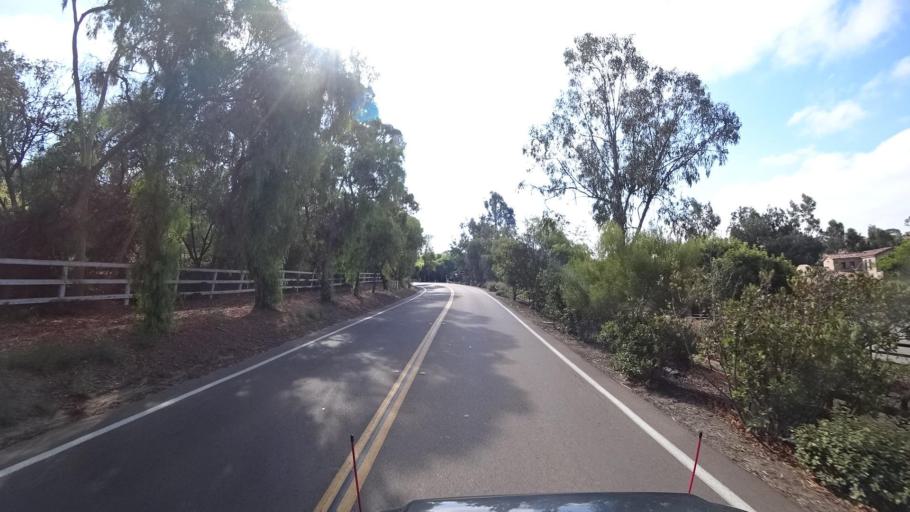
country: US
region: California
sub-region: San Diego County
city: Rancho Santa Fe
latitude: 33.0454
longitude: -117.2132
